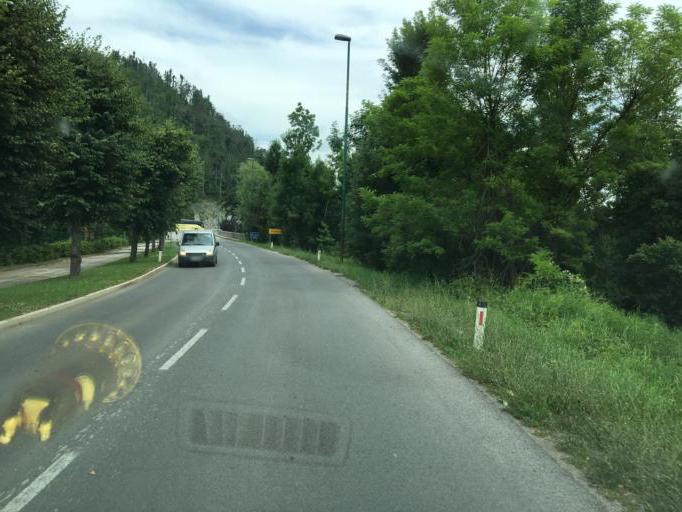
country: SI
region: Postojna
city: Postojna
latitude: 45.7803
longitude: 14.2035
